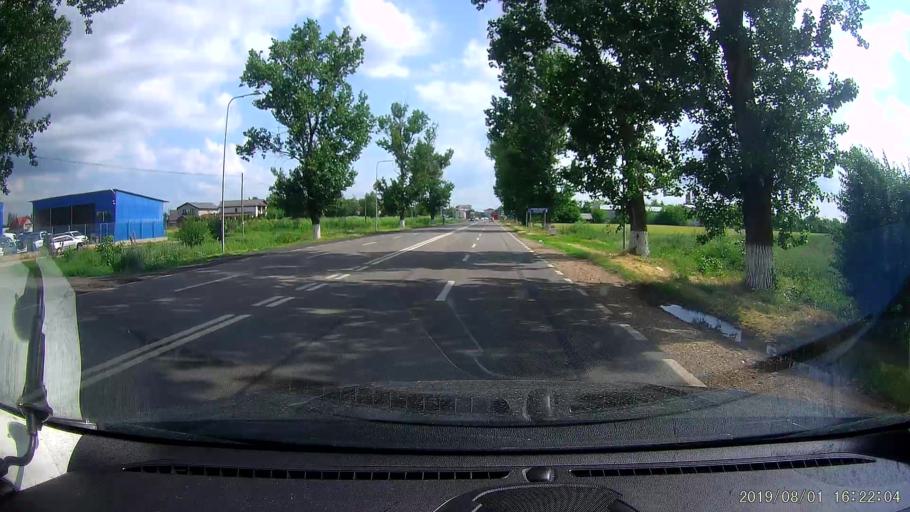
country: RO
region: Calarasi
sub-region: Municipiul Calarasi
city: Calarasi
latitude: 44.2082
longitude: 27.3383
